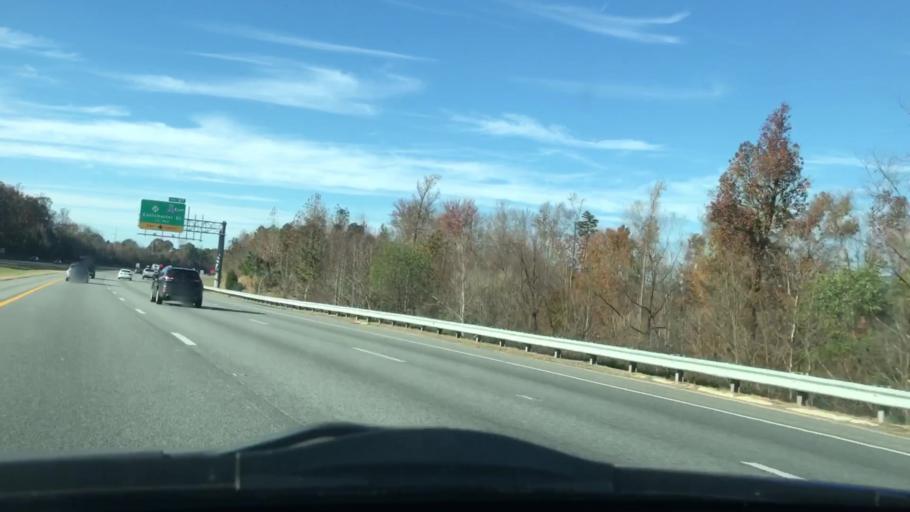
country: US
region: North Carolina
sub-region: Guilford County
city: High Point
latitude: 35.9909
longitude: -79.9825
